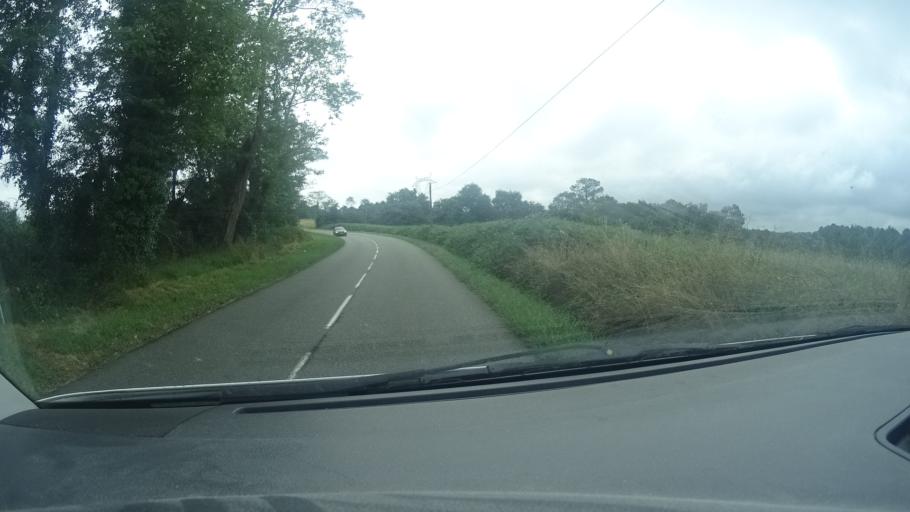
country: FR
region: Aquitaine
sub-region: Departement des Pyrenees-Atlantiques
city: Mont
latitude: 43.4894
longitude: -0.6750
